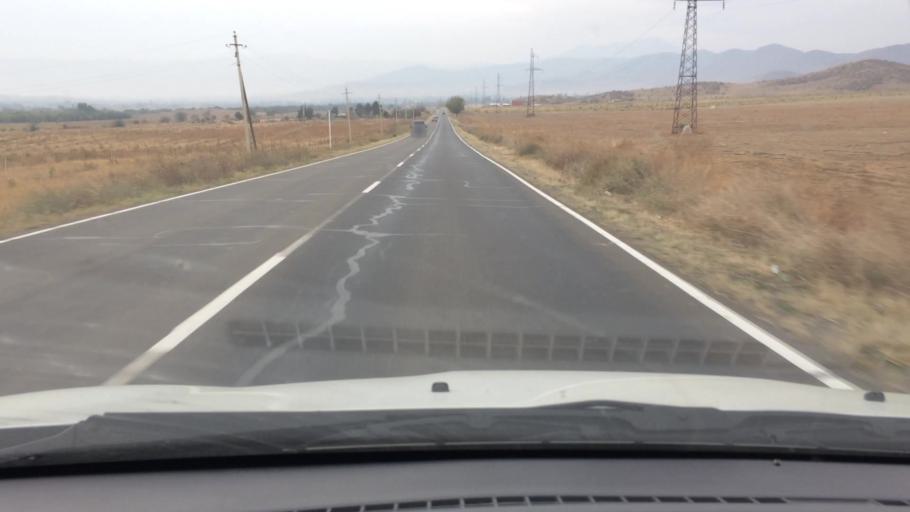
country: GE
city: Naghvarevi
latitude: 41.3518
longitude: 44.8202
